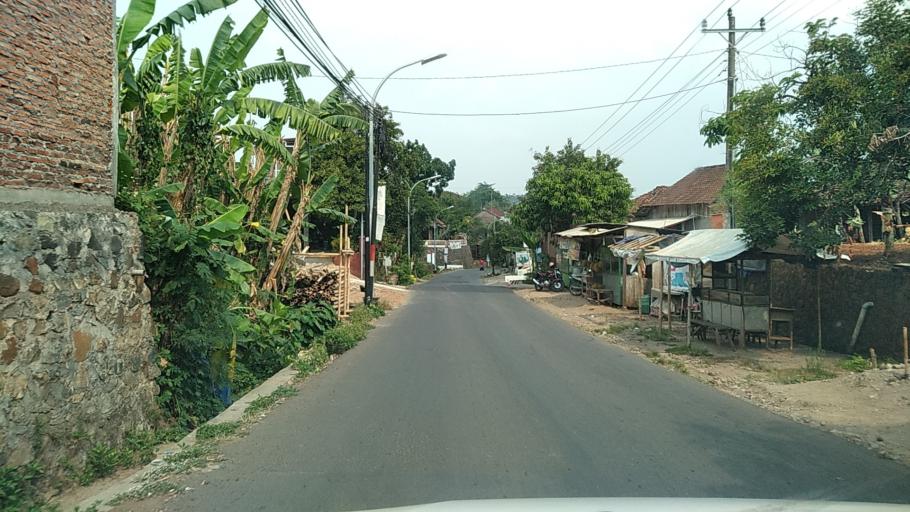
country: ID
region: Central Java
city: Semarang
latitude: -7.0044
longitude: 110.3189
